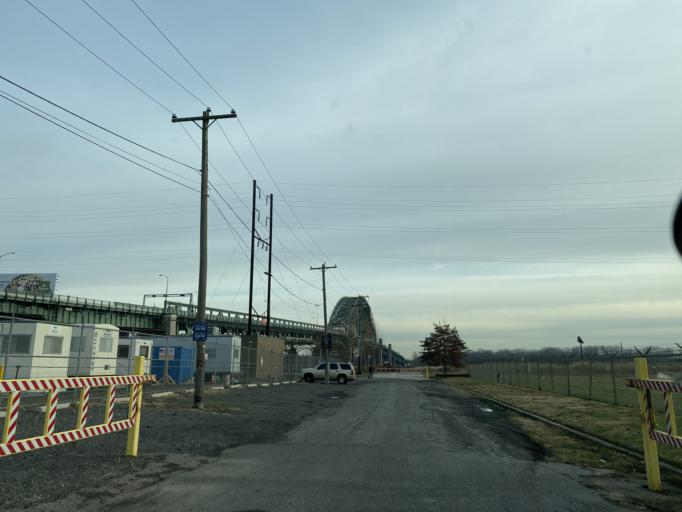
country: US
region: New Jersey
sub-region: Burlington County
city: Palmyra
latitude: 40.0156
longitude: -75.0466
